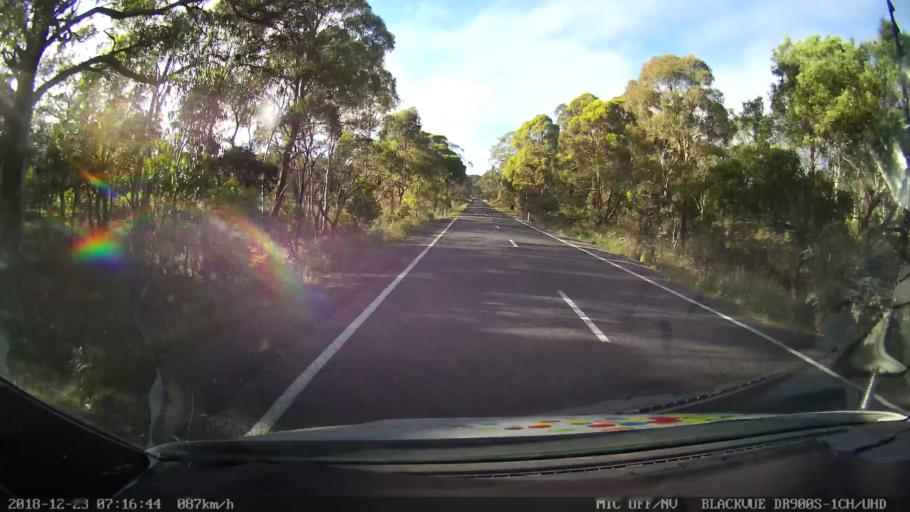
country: AU
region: New South Wales
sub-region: Bellingen
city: Dorrigo
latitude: -30.4596
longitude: 152.3081
